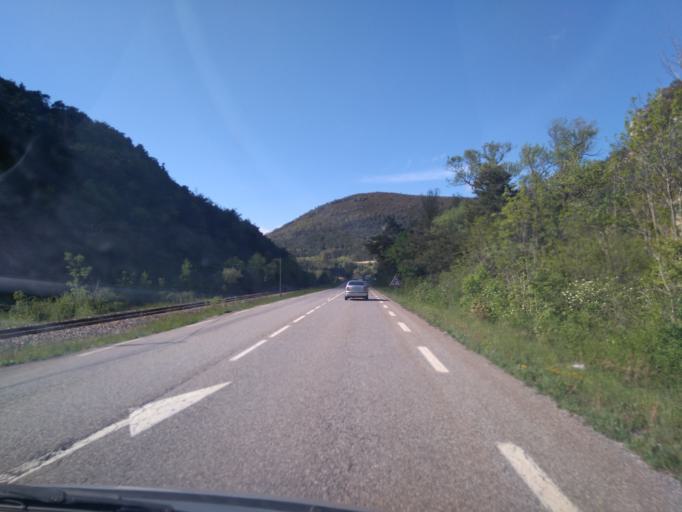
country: FR
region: Provence-Alpes-Cote d'Azur
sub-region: Departement des Hautes-Alpes
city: Veynes
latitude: 44.6087
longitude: 5.7079
